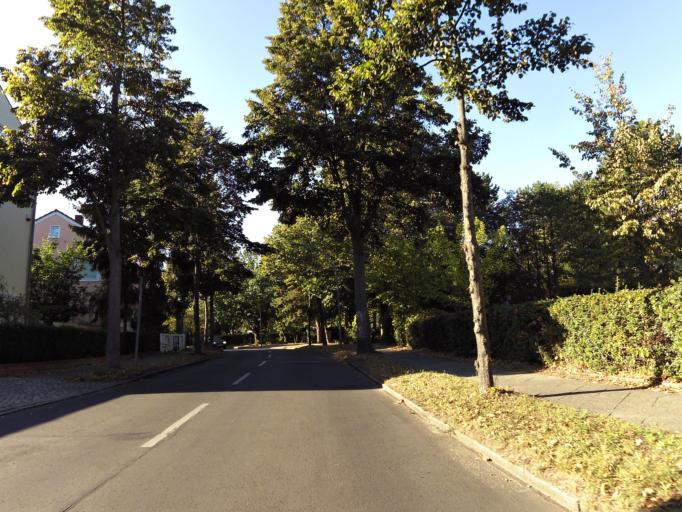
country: DE
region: Berlin
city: Dahlem
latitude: 52.4489
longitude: 13.2752
